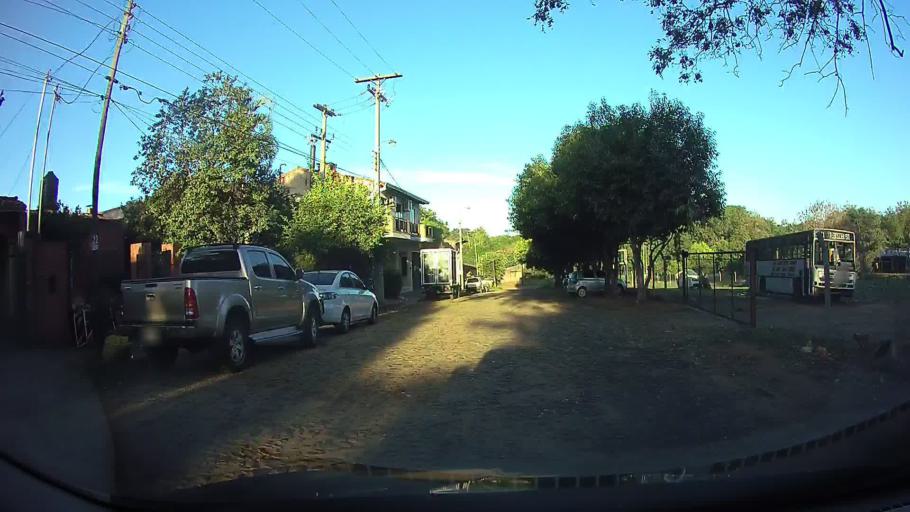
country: PY
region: Central
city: San Lorenzo
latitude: -25.2625
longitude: -57.4881
